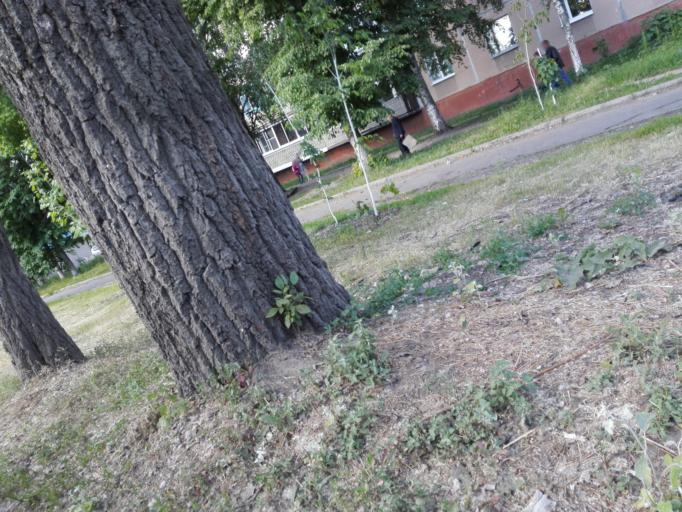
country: RU
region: Orjol
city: Orel
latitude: 52.9572
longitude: 36.0727
